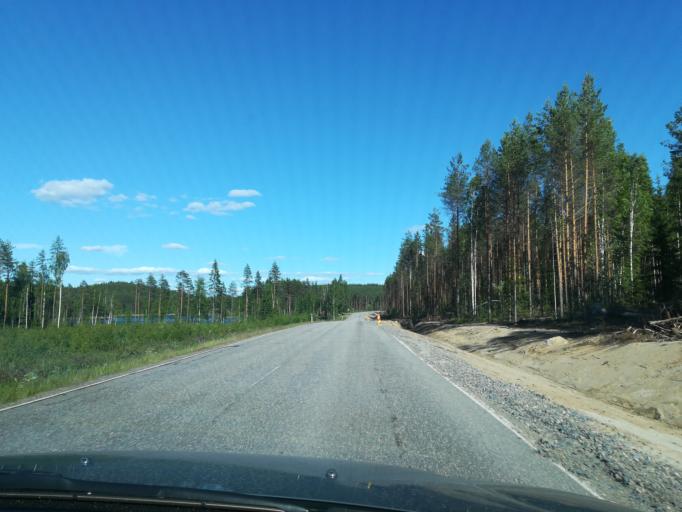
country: FI
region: Southern Savonia
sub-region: Mikkeli
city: Puumala
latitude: 61.4645
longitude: 28.3829
